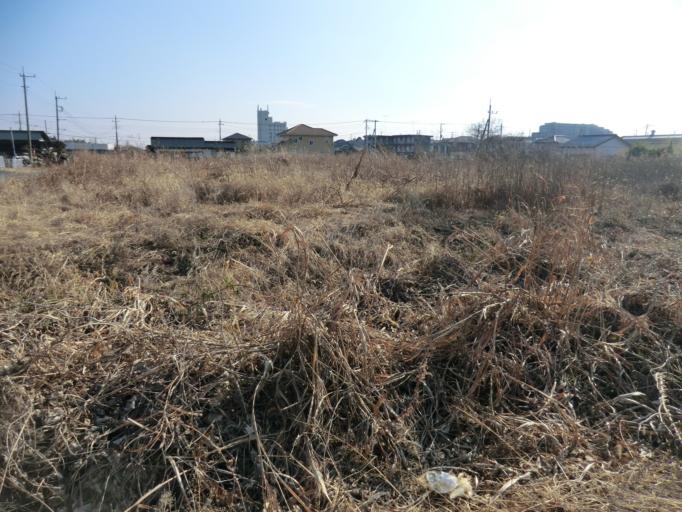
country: JP
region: Ibaraki
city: Naka
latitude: 36.0899
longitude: 140.1243
